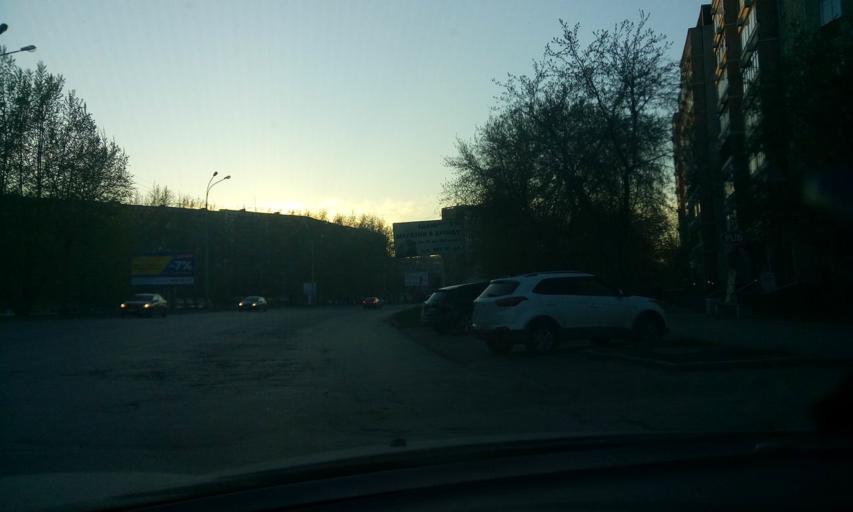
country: RU
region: Sverdlovsk
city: Yekaterinburg
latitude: 56.8356
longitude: 60.6823
